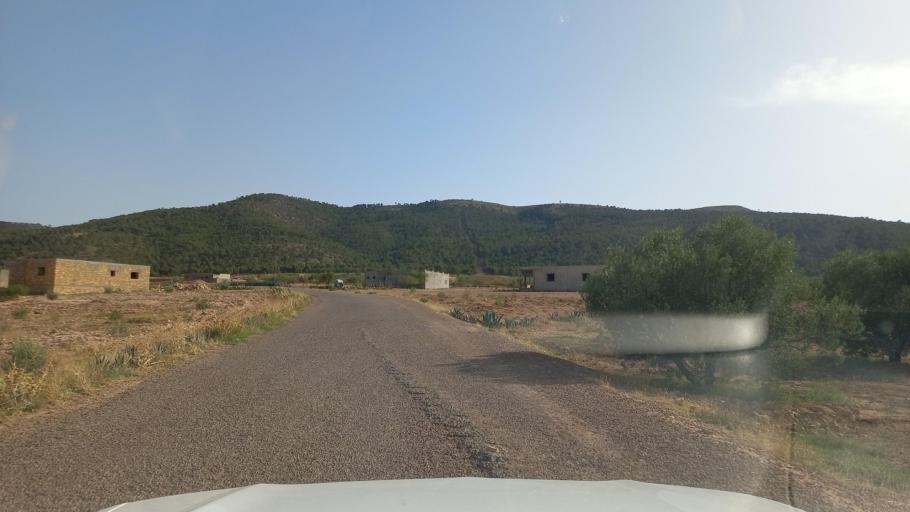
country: TN
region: Al Qasrayn
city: Kasserine
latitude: 35.3407
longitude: 8.8346
